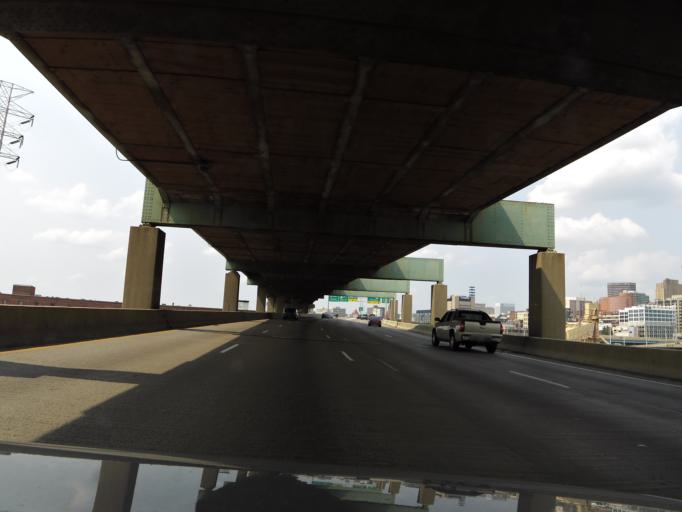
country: US
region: Kentucky
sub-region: Kenton County
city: Covington
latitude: 39.0939
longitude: -84.5225
